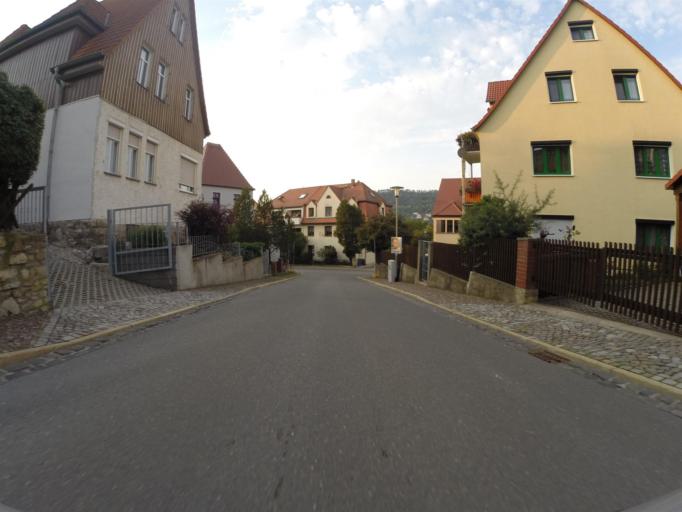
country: DE
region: Thuringia
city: Jena
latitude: 50.9284
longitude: 11.5720
